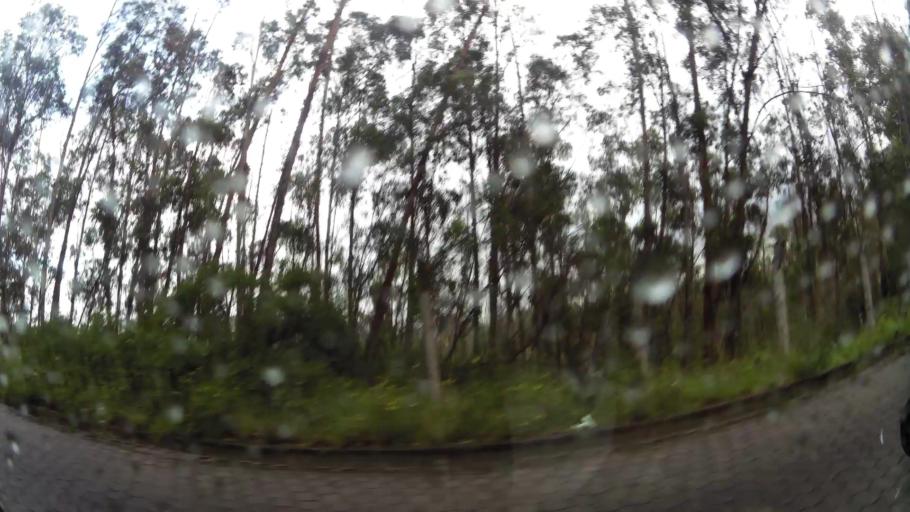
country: EC
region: Pichincha
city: Quito
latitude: -0.0902
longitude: -78.4961
